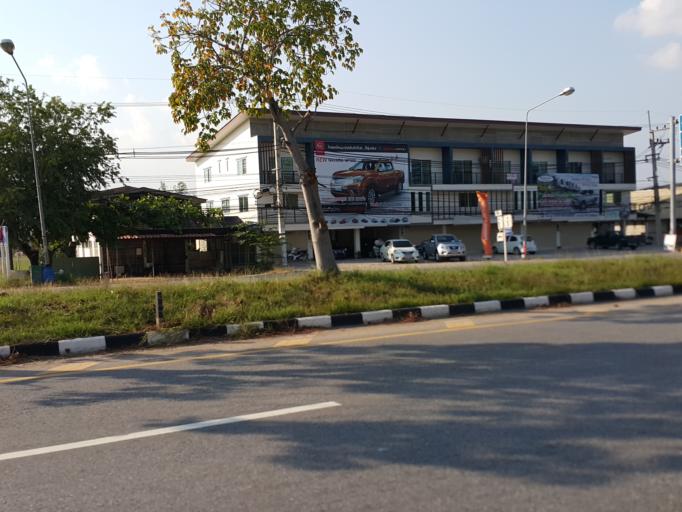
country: TH
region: Lampang
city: Thoen
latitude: 17.6275
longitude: 99.2383
